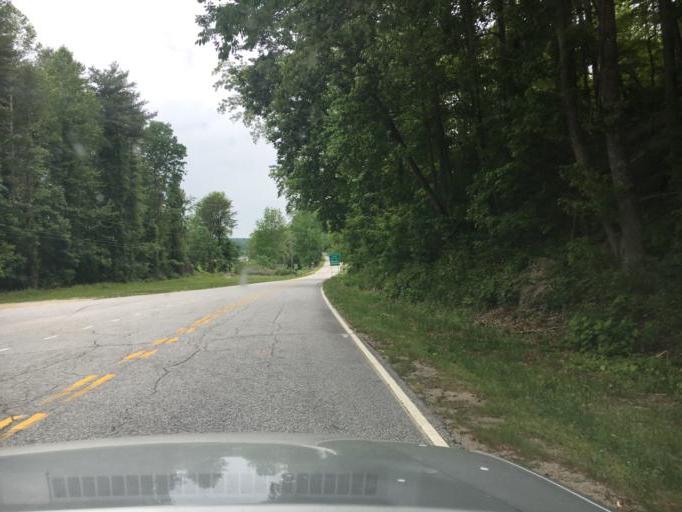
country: US
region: South Carolina
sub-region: Greenville County
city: Tigerville
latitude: 35.1335
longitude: -82.4206
